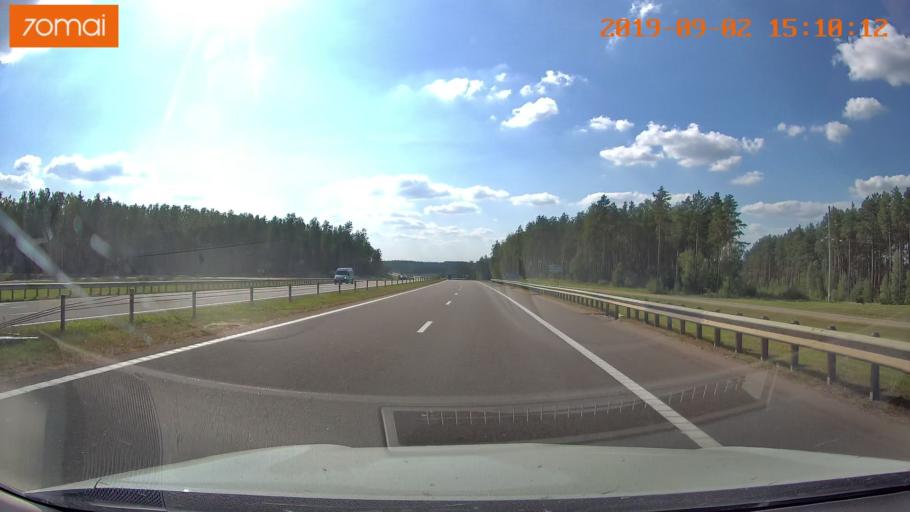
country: BY
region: Mogilev
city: Byalynichy
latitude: 53.9842
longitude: 29.7918
